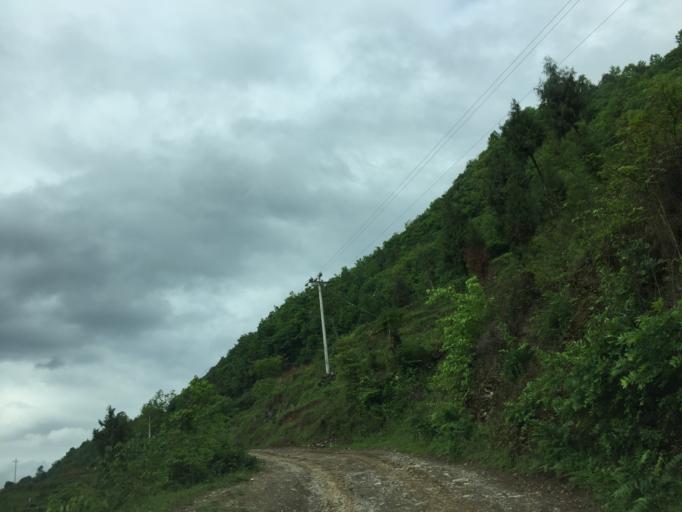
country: CN
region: Guizhou Sheng
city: Xujiaba
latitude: 27.8478
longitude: 108.2173
